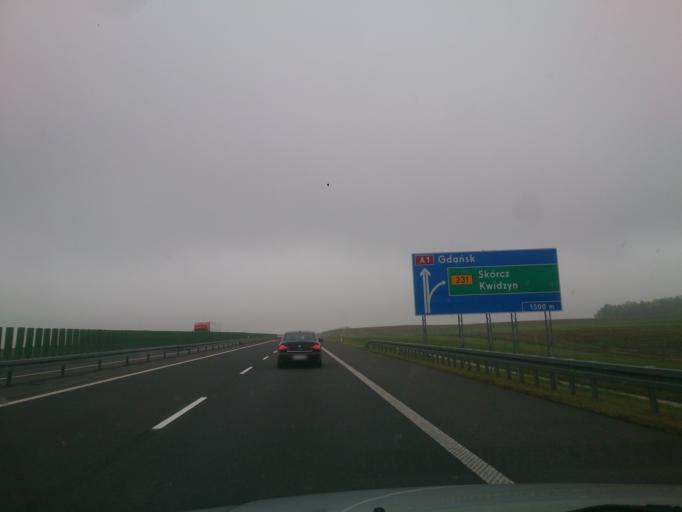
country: PL
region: Pomeranian Voivodeship
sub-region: Powiat starogardzki
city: Smetowo Graniczne
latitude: 53.7181
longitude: 18.6297
